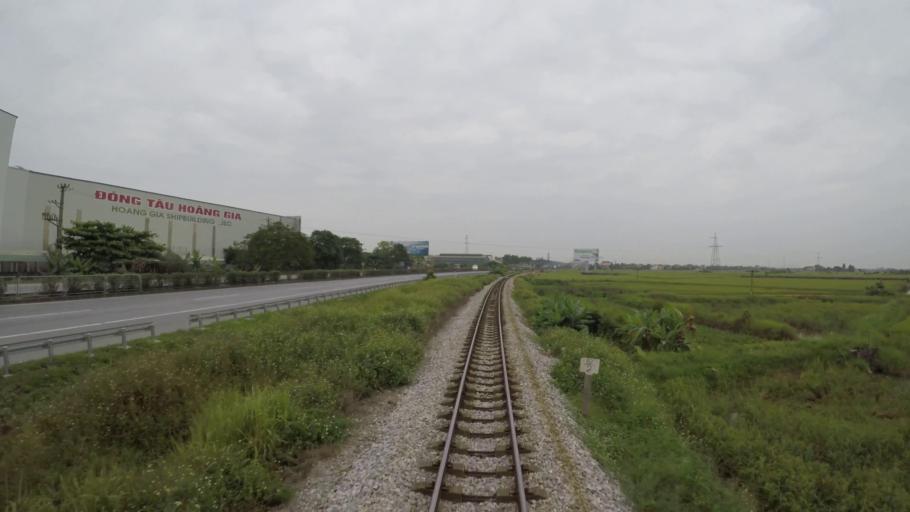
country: VN
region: Hai Duong
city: Phu Thai
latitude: 20.9501
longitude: 106.5327
